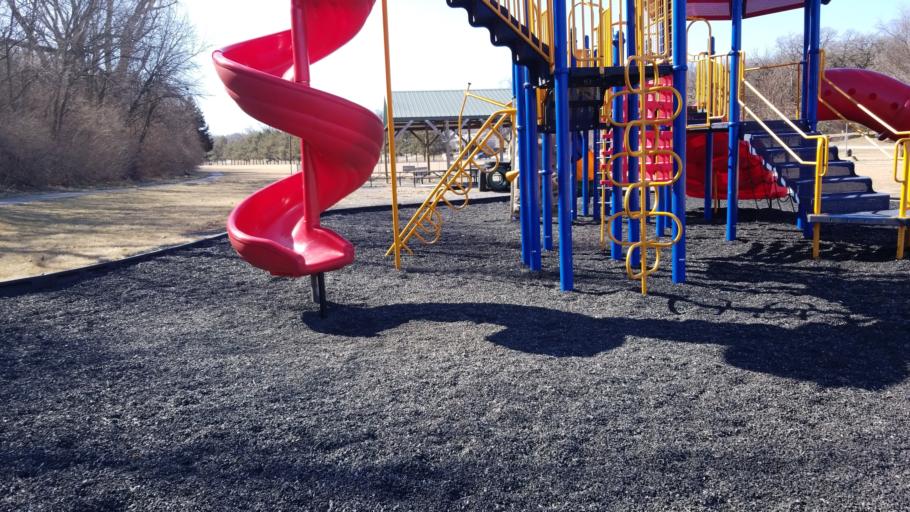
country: US
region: Nebraska
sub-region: Cass County
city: Plattsmouth
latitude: 41.0047
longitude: -95.8844
